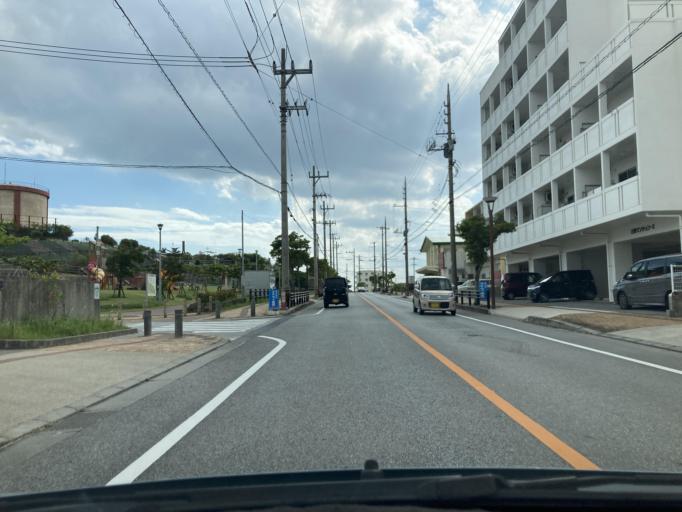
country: JP
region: Okinawa
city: Ginowan
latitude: 26.2477
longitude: 127.7729
